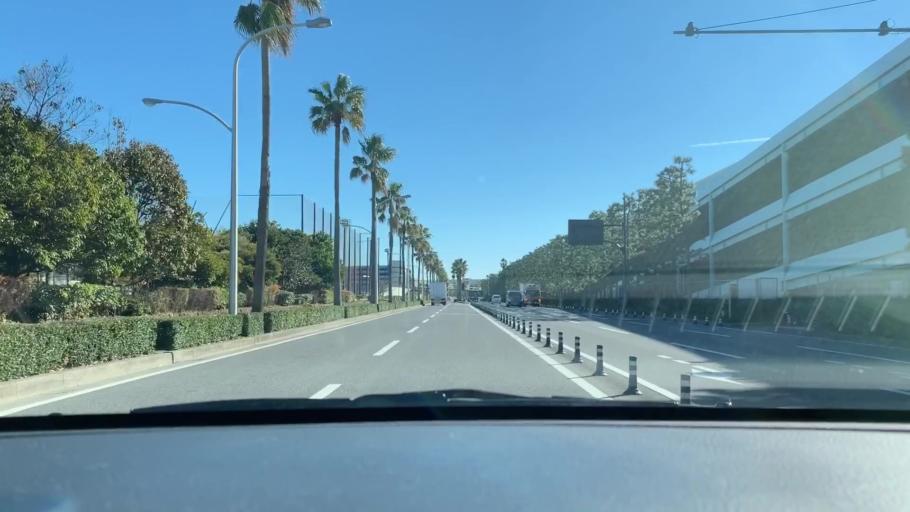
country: JP
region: Tokyo
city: Urayasu
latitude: 35.6292
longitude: 139.8891
